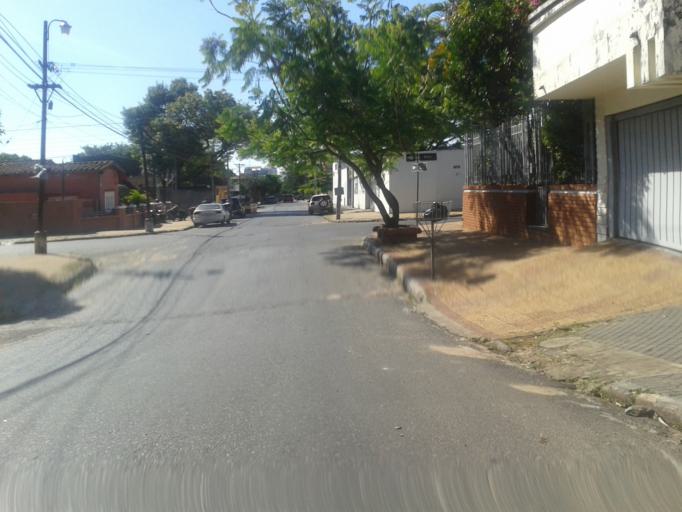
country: PY
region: Asuncion
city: Asuncion
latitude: -25.2952
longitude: -57.6372
